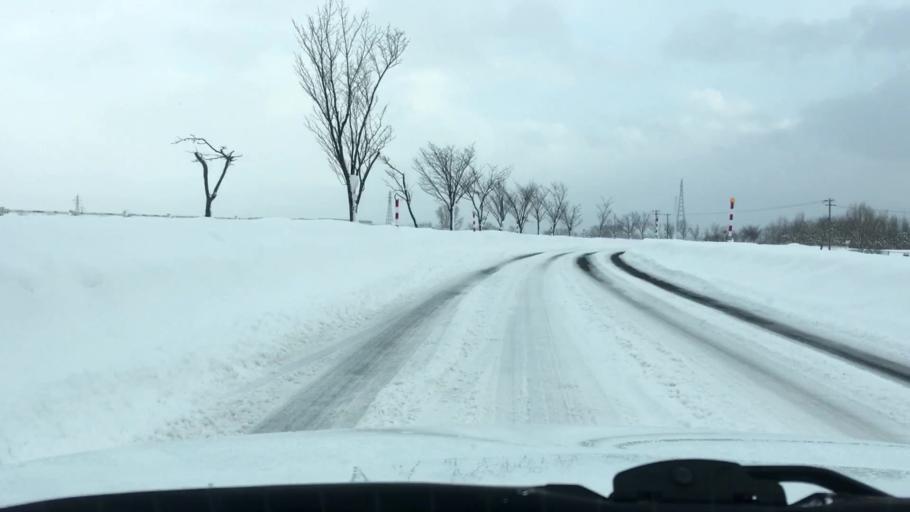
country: JP
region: Aomori
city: Hirosaki
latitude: 40.6517
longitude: 140.4731
